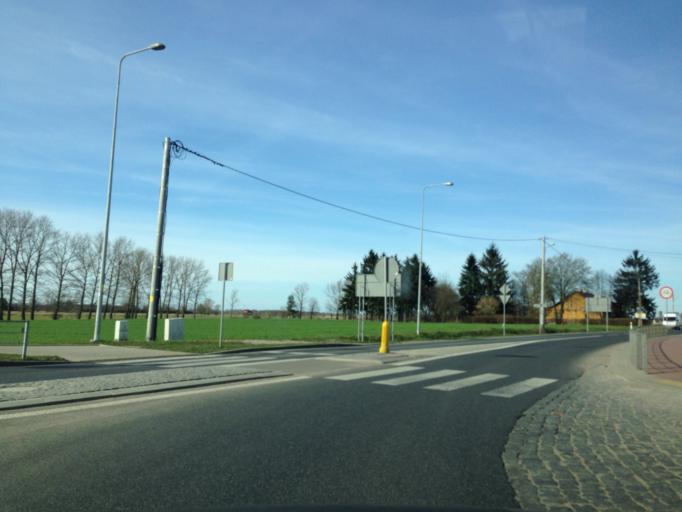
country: PL
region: Lodz Voivodeship
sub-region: Powiat poddebicki
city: Wartkowice
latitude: 51.9730
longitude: 19.0190
